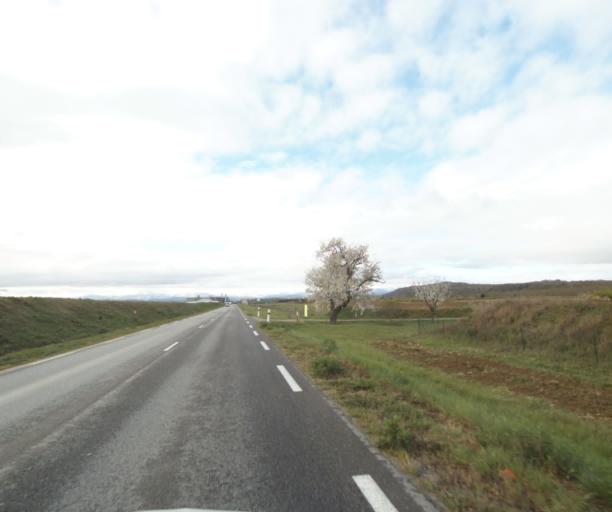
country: FR
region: Midi-Pyrenees
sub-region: Departement de l'Ariege
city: Saverdun
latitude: 43.2088
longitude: 1.6084
